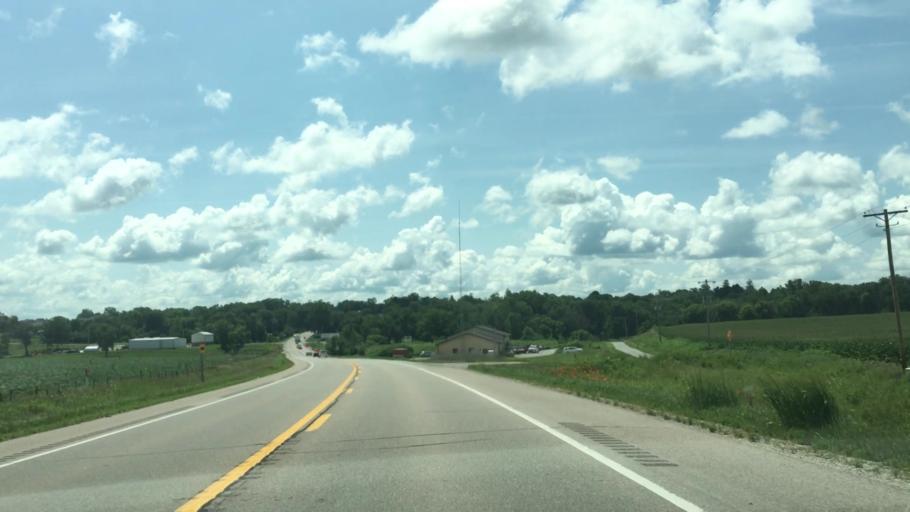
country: US
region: Iowa
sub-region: Johnson County
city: Solon
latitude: 41.8160
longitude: -91.4958
